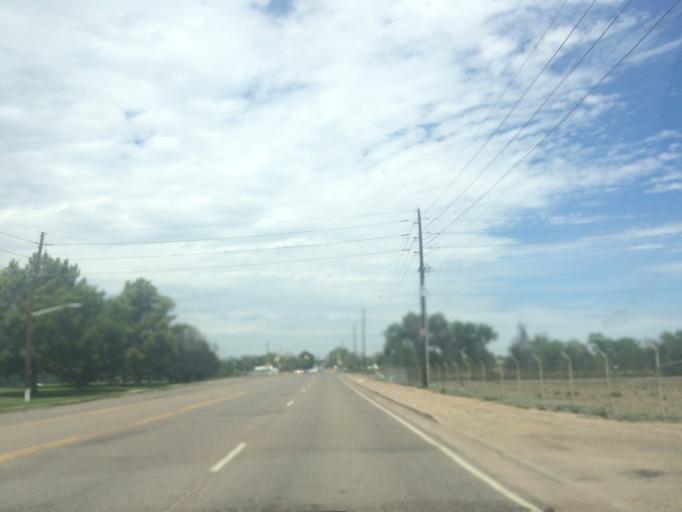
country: US
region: Colorado
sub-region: Adams County
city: Welby
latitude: 39.8268
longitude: -104.9591
